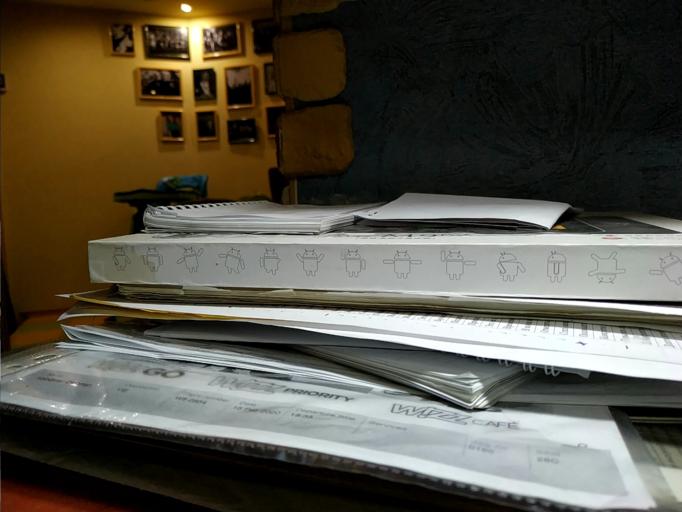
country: RU
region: Arkhangelskaya
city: Konevo
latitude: 62.1221
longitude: 38.9570
